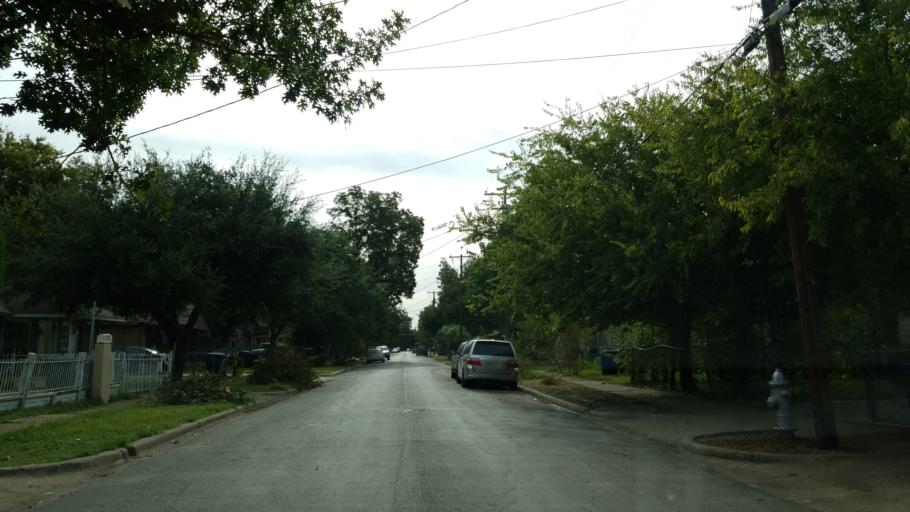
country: US
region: Texas
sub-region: Dallas County
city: Dallas
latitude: 32.7842
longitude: -96.7197
